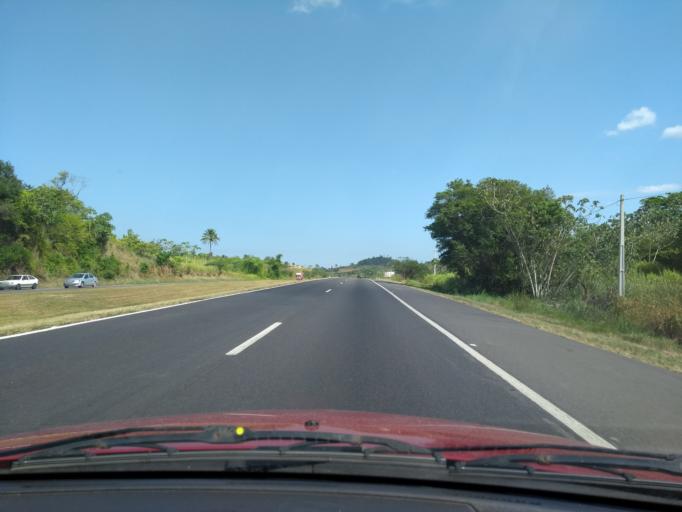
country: BR
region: Bahia
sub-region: Sao Sebastiao Do Passe
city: Sao Sebastiao do Passe
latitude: -12.5932
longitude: -38.5176
